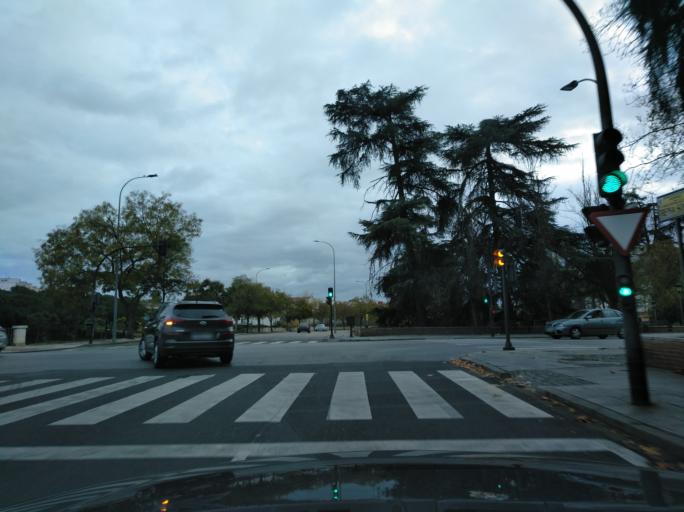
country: ES
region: Extremadura
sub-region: Provincia de Badajoz
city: Badajoz
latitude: 38.8786
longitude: -6.9633
